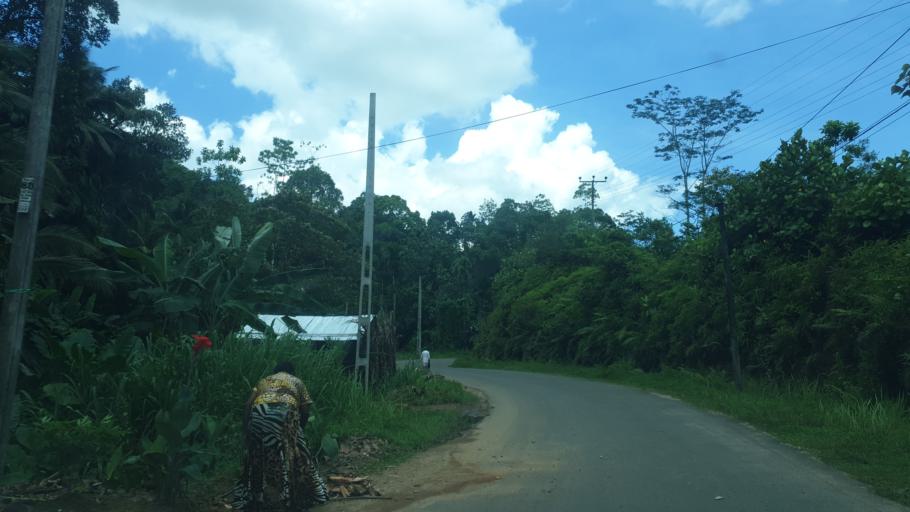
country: LK
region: Sabaragamuwa
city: Ratnapura
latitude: 6.4800
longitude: 80.4149
